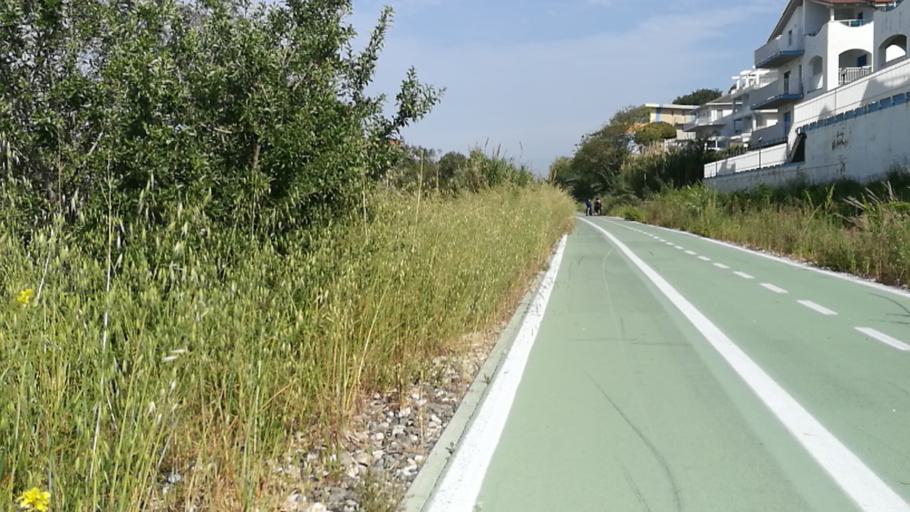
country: IT
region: Abruzzo
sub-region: Provincia di Chieti
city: Villalfonsina
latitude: 42.2085
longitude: 14.5952
